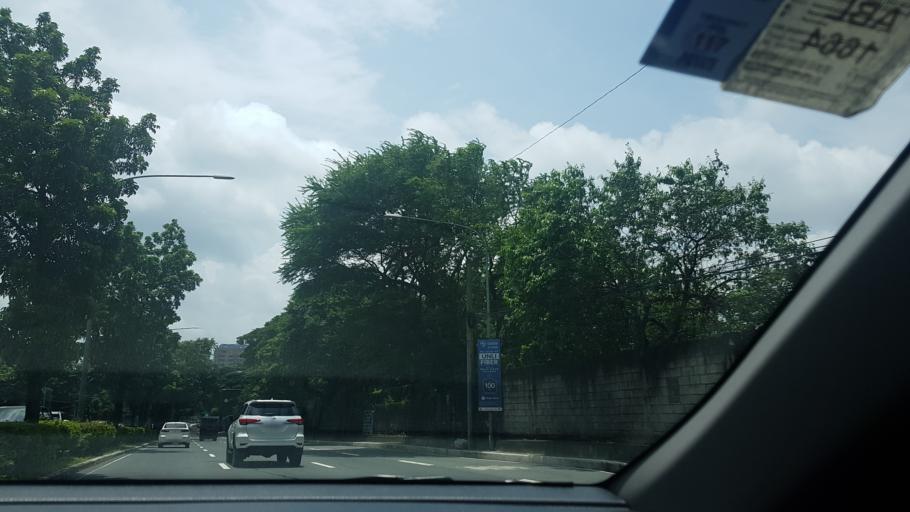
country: PH
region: Metro Manila
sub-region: Pasig
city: Pasig City
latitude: 14.5981
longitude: 121.0517
